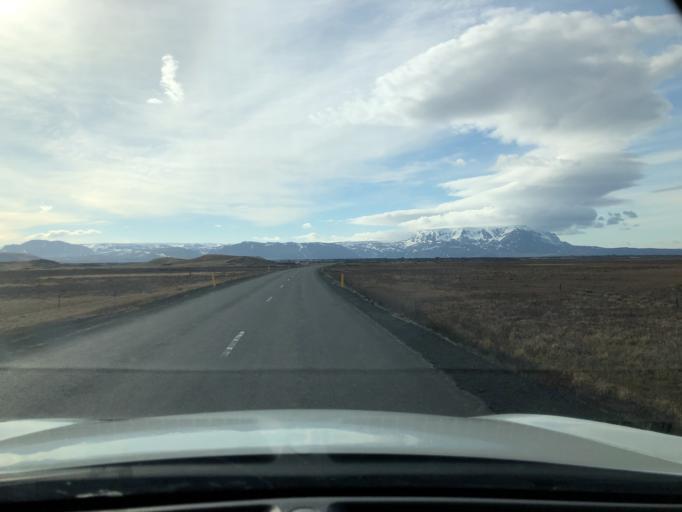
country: IS
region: Northeast
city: Laugar
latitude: 65.5595
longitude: -16.9940
